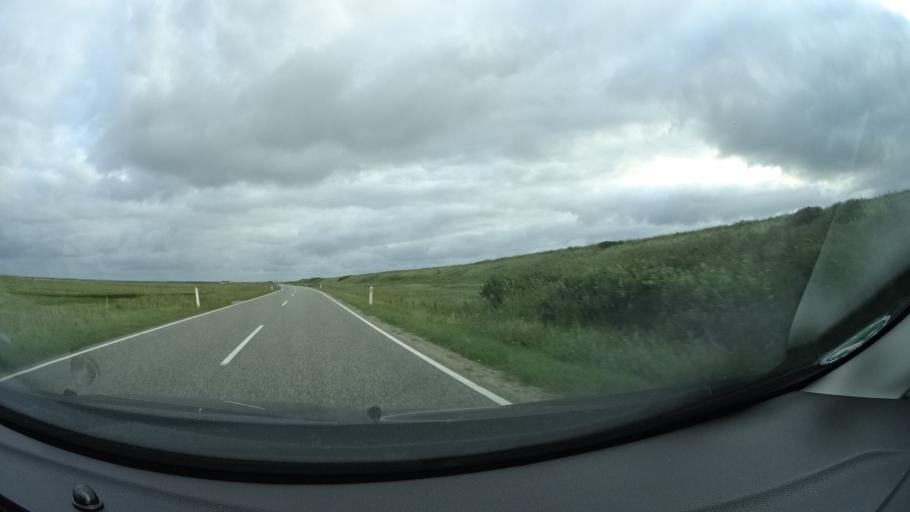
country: DK
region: Central Jutland
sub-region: Lemvig Kommune
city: Harboore
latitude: 56.3954
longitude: 8.1214
